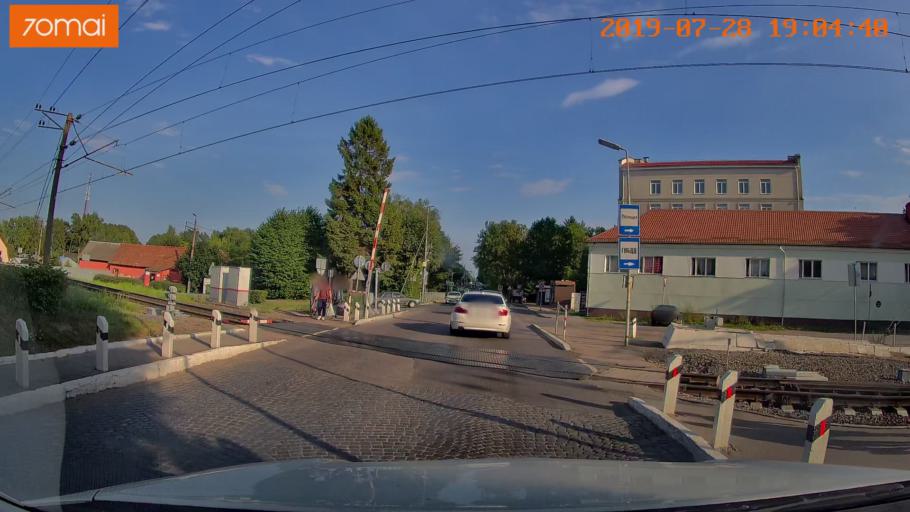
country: RU
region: Kaliningrad
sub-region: Gorod Svetlogorsk
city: Svetlogorsk
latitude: 54.9335
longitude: 20.1619
